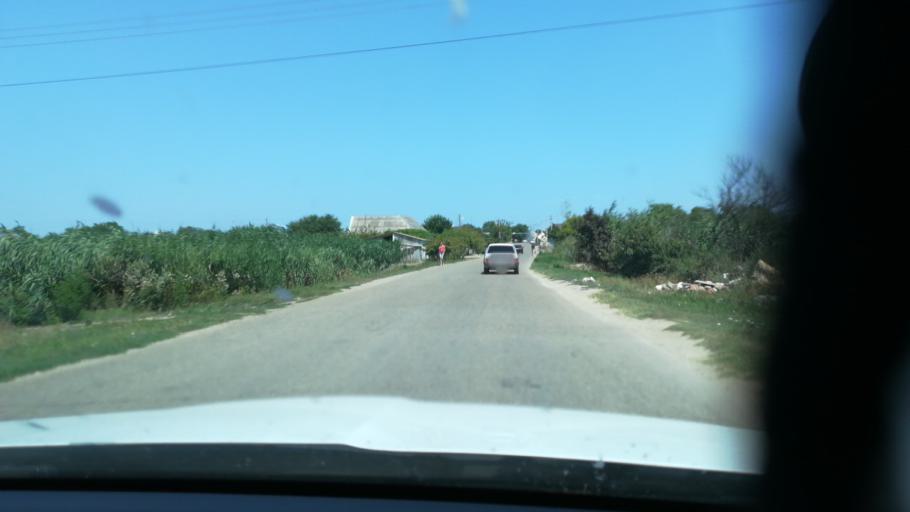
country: RU
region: Krasnodarskiy
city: Starotitarovskaya
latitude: 45.2106
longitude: 37.1450
